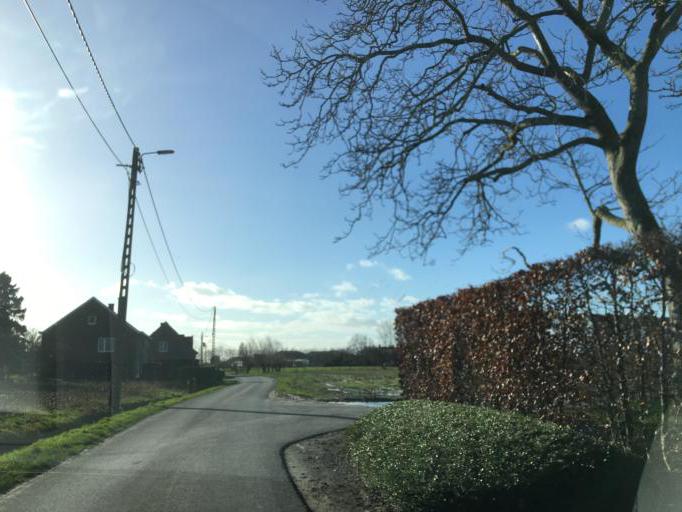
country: BE
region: Flanders
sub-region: Provincie West-Vlaanderen
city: Ardooie
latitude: 50.9681
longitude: 3.1667
